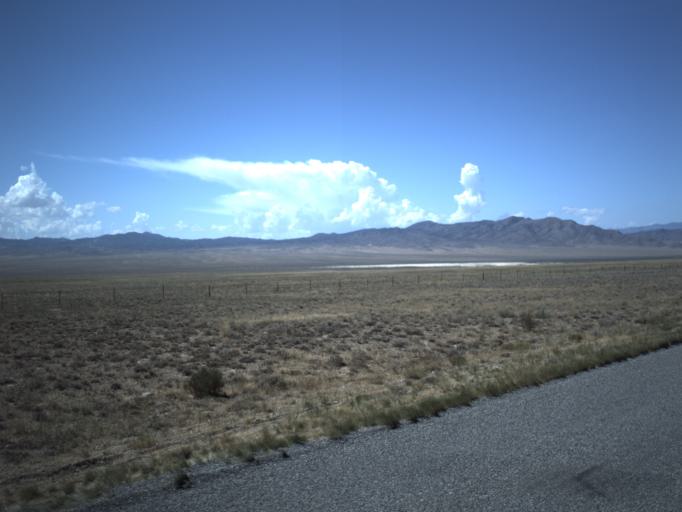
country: US
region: Utah
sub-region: Beaver County
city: Milford
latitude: 39.0502
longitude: -113.7851
